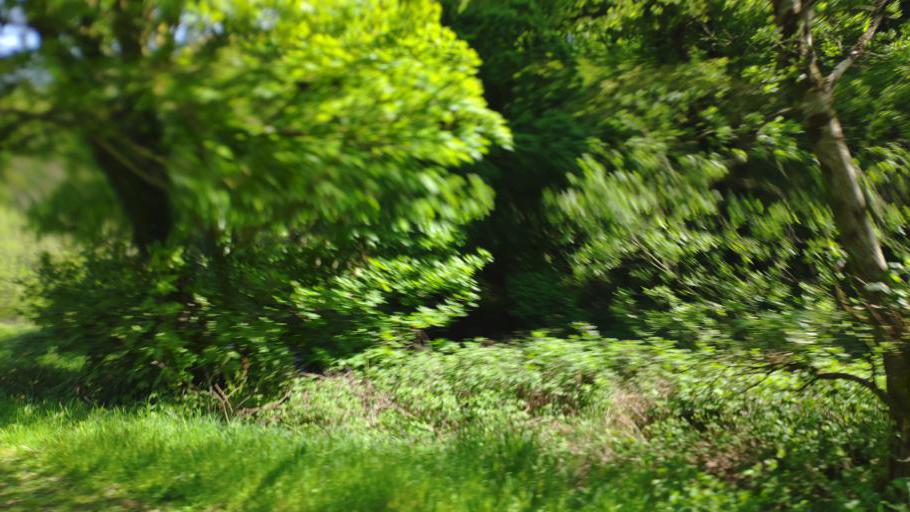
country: IE
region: Munster
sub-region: County Cork
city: Blarney
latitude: 51.9436
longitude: -8.5658
